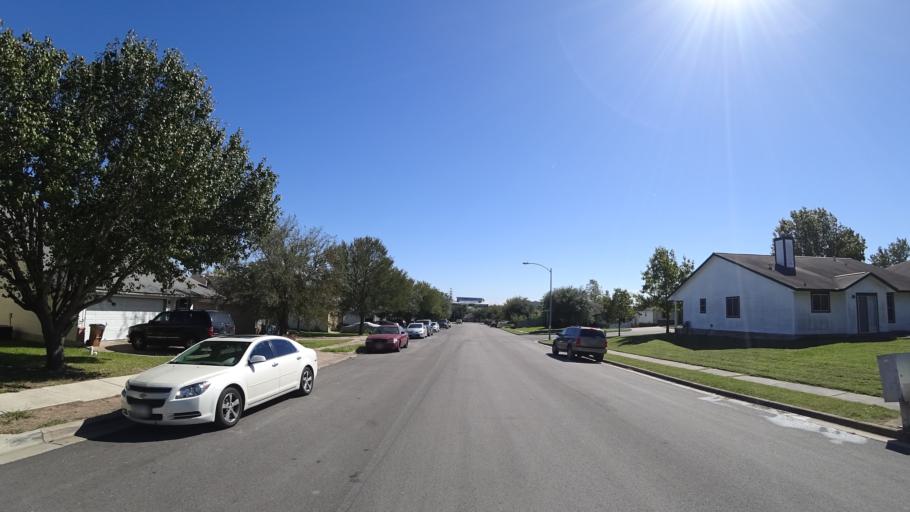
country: US
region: Texas
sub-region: Travis County
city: Hornsby Bend
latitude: 30.3038
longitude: -97.6388
